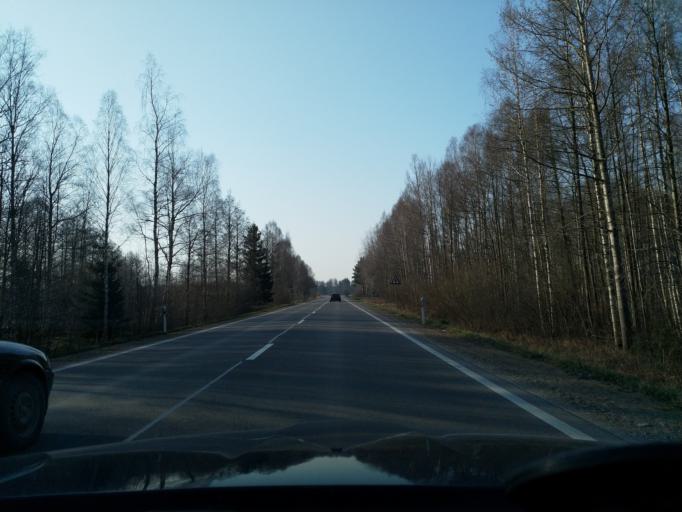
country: LV
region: Rucavas
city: Rucava
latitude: 56.2391
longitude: 21.1056
